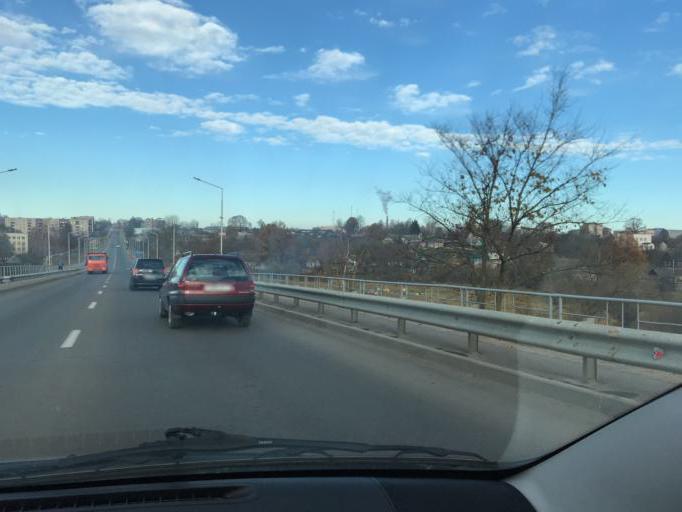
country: BY
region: Vitebsk
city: Haradok
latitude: 55.4650
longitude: 29.9801
